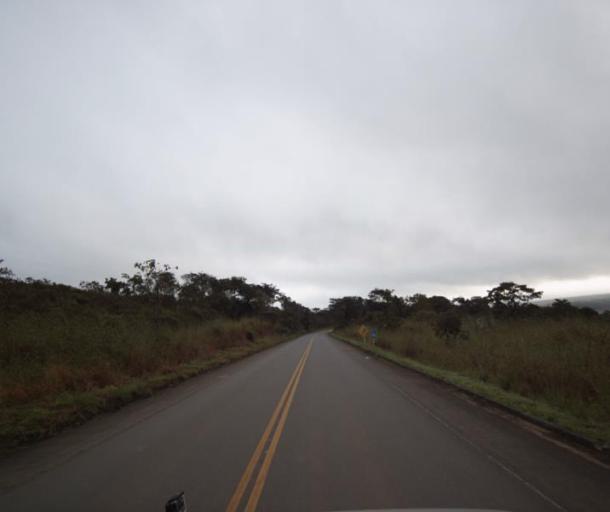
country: BR
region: Goias
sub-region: Pirenopolis
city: Pirenopolis
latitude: -15.8655
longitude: -48.7733
